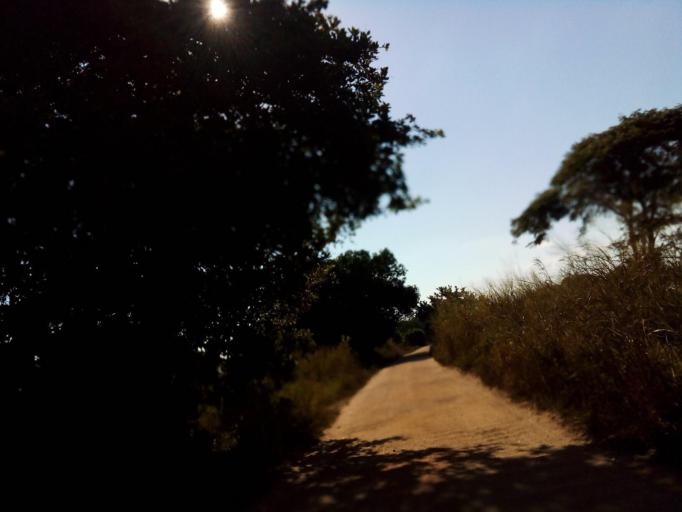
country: MZ
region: Zambezia
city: Quelimane
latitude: -17.5296
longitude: 36.6187
